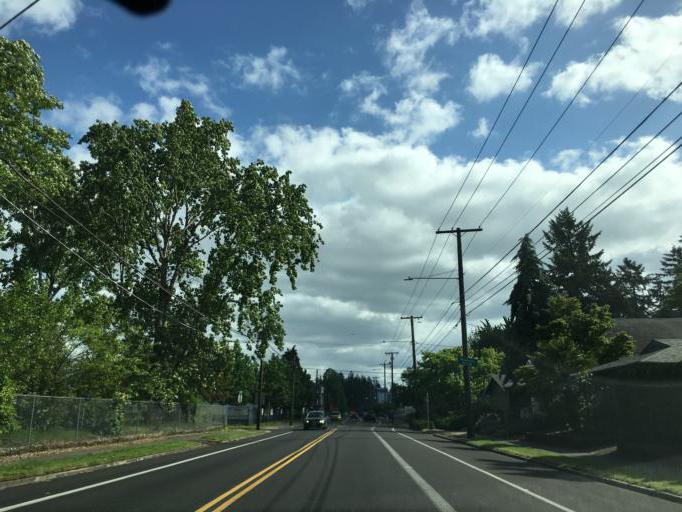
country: US
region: Oregon
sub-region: Multnomah County
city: Lents
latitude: 45.4806
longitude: -122.6088
